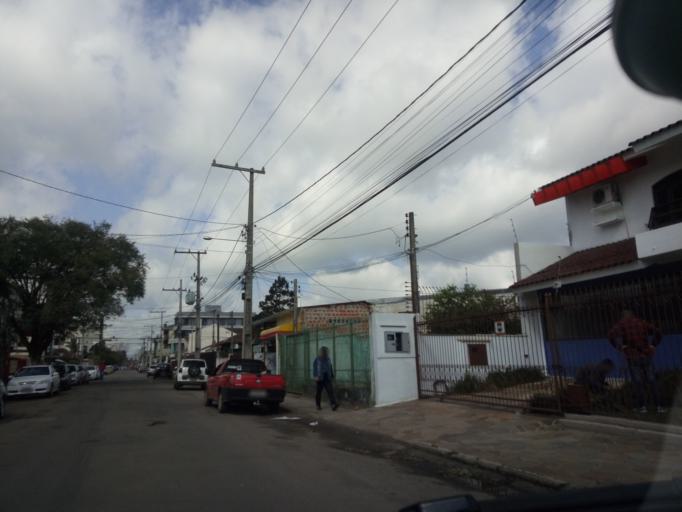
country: BR
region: Rio Grande do Sul
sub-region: Santa Maria
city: Santa Maria
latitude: -29.7020
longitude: -53.7225
